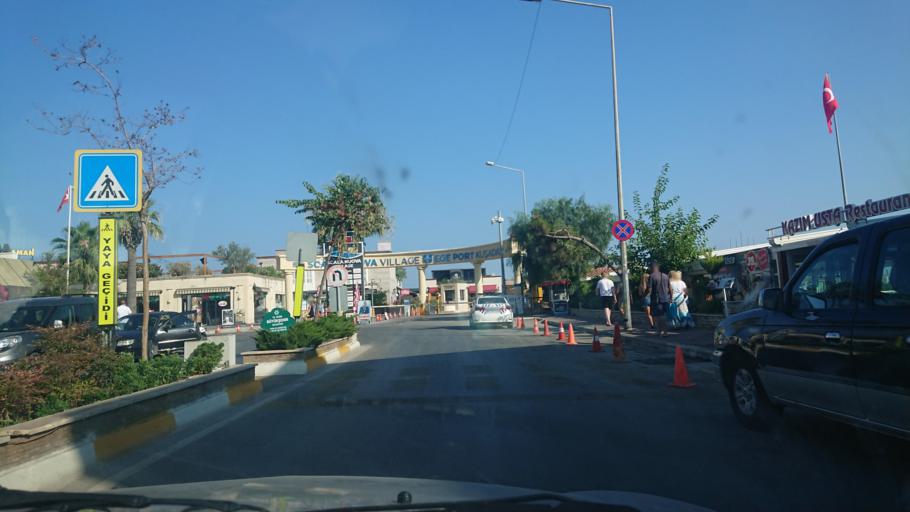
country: TR
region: Aydin
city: Kusadasi
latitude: 37.8610
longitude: 27.2557
